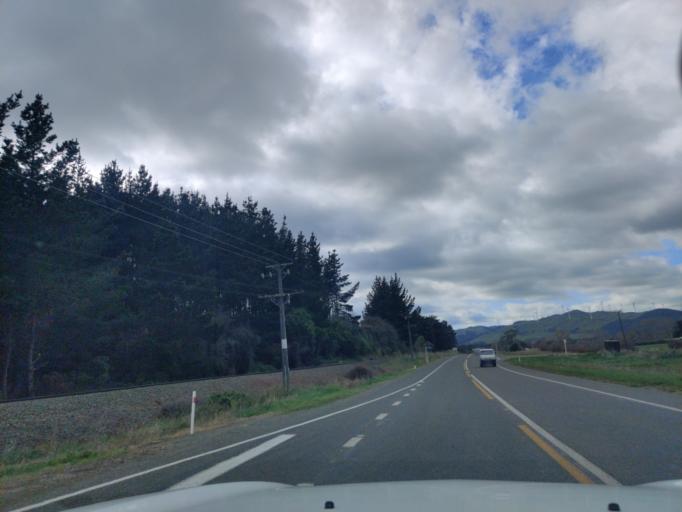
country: NZ
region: Manawatu-Wanganui
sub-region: Palmerston North City
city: Palmerston North
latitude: -40.2998
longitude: 175.7404
